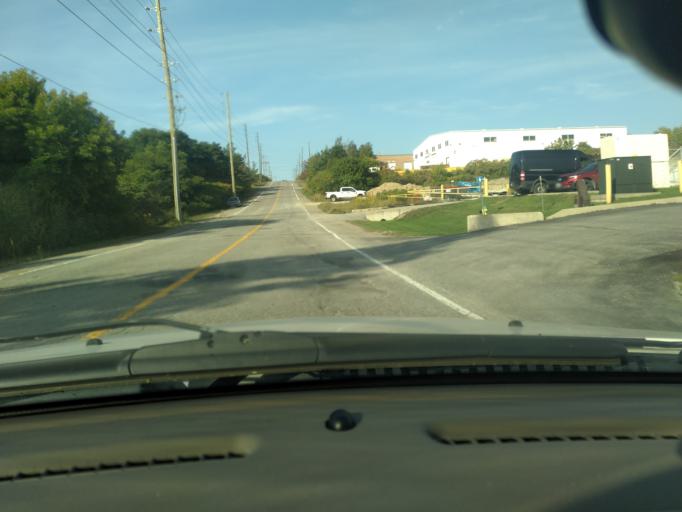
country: CA
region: Ontario
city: Innisfil
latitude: 44.3248
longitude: -79.6763
